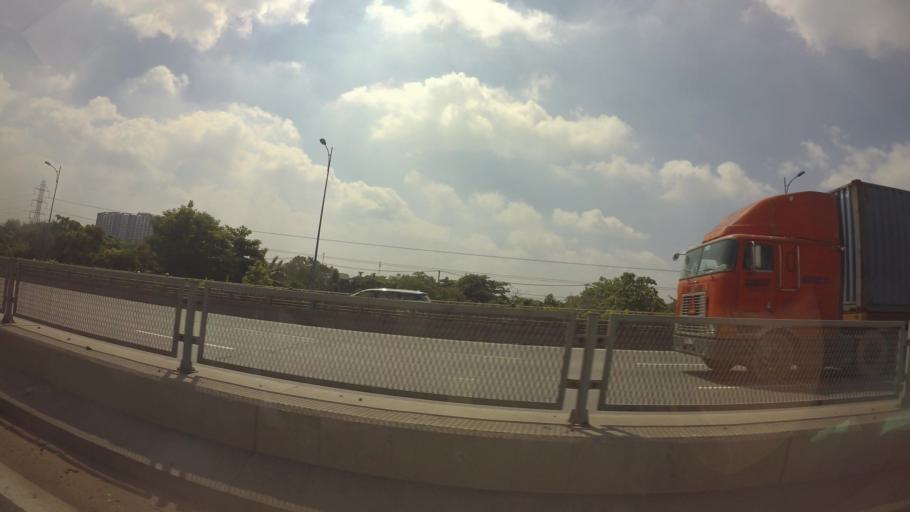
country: VN
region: Ho Chi Minh City
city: Quan Hai
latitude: 10.8143
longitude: 106.7572
